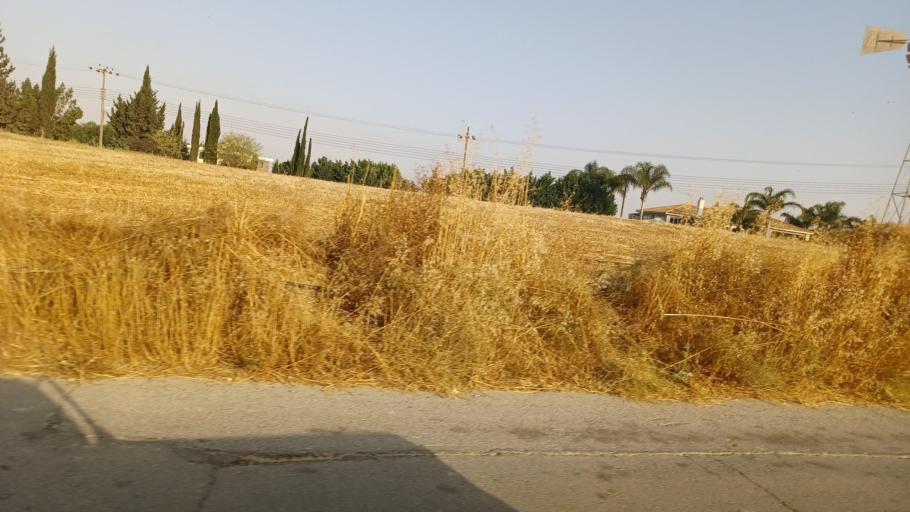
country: CY
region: Ammochostos
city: Paralimni
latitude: 35.0296
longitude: 33.9783
